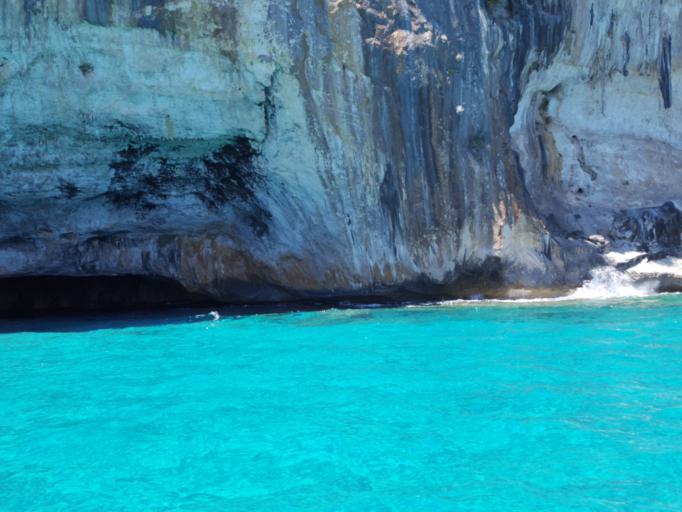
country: IT
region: Sardinia
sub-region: Provincia di Nuoro
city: Cala Gonone
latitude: 40.2469
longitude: 9.6234
